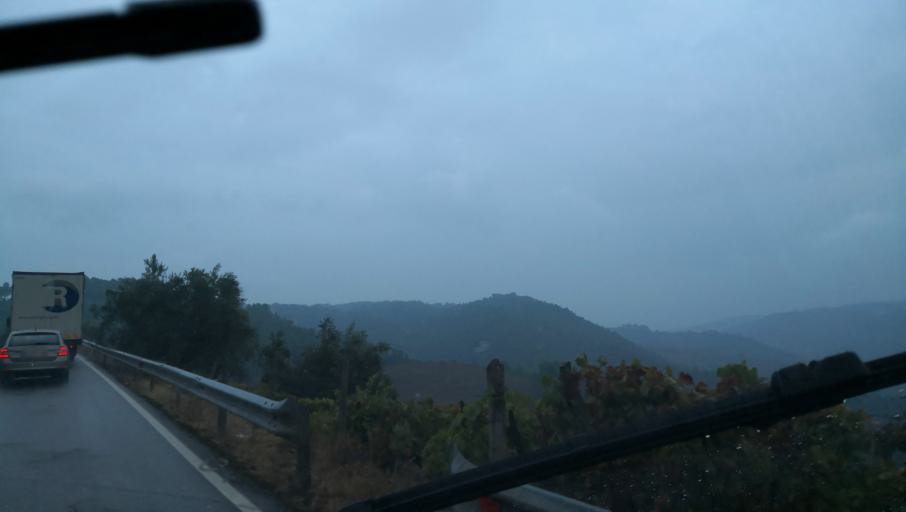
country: PT
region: Vila Real
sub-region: Vila Real
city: Vila Real
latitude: 41.2343
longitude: -7.7272
